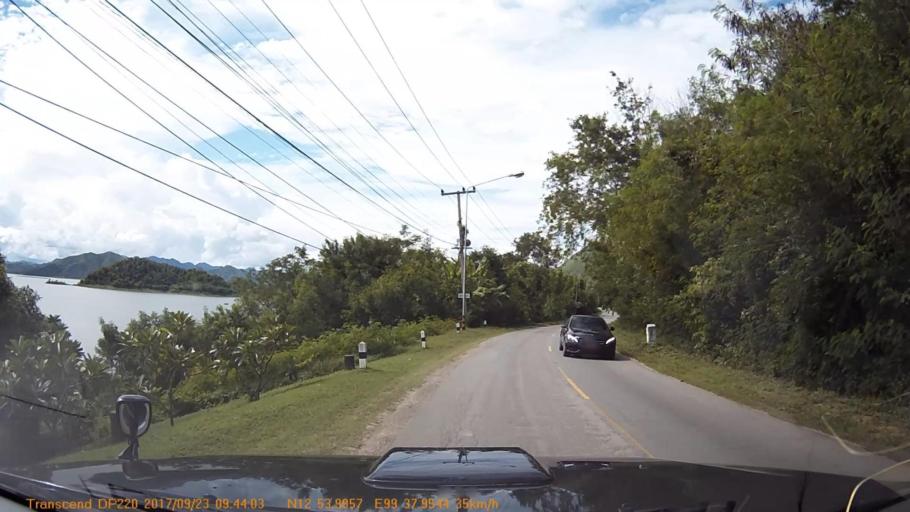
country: TH
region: Phetchaburi
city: Kaeng Krachan
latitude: 12.9000
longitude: 99.6326
